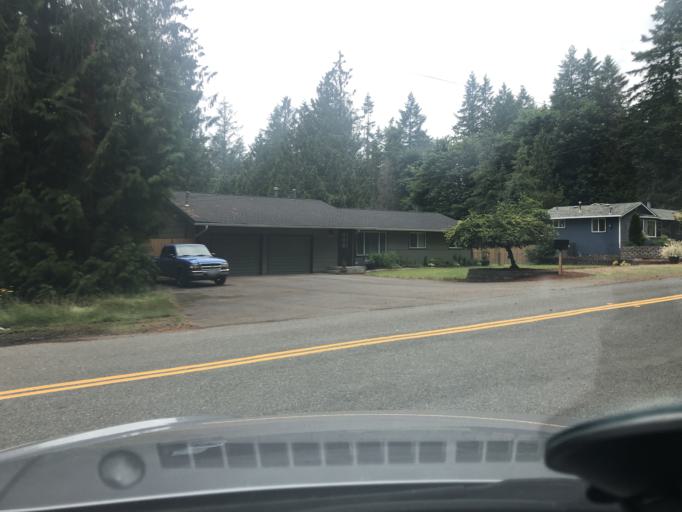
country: US
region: Washington
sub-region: King County
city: Black Diamond
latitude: 47.3223
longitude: -122.0387
